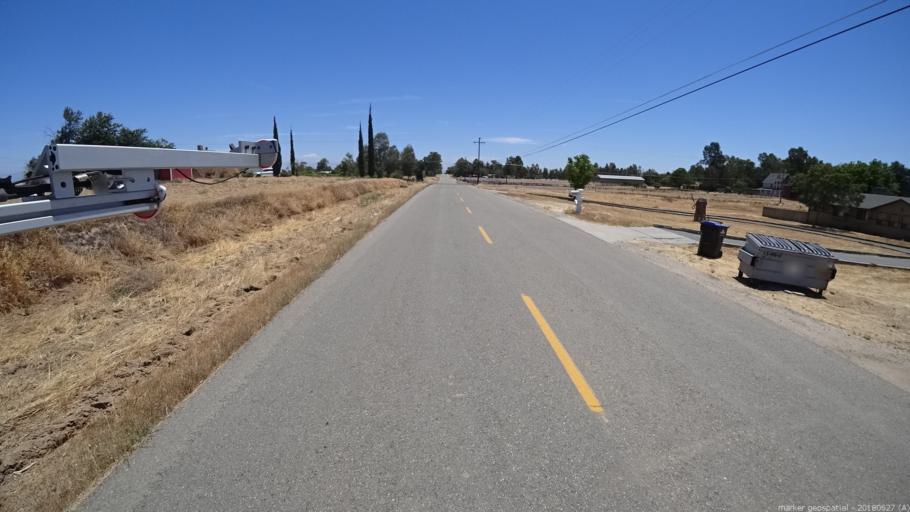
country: US
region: California
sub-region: Madera County
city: Bonadelle Ranchos-Madera Ranchos
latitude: 36.9448
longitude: -119.9133
